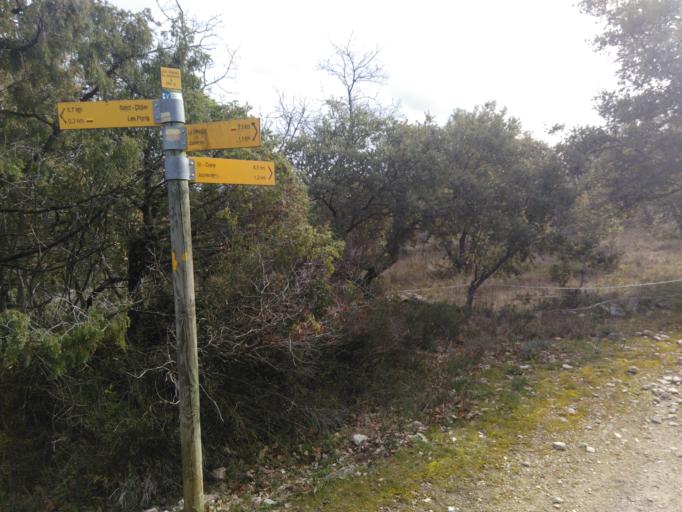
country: FR
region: Provence-Alpes-Cote d'Azur
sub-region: Departement du Vaucluse
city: Venasque
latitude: 43.9960
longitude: 5.1376
